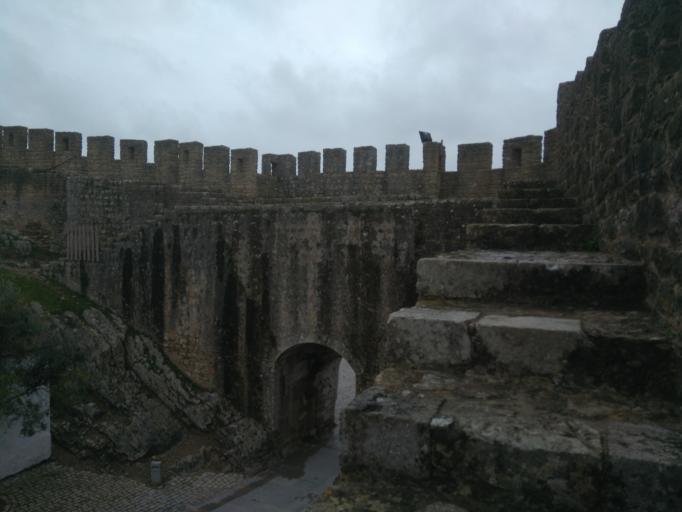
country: PT
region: Leiria
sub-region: Obidos
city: Obidos
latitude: 39.3644
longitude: -9.1576
